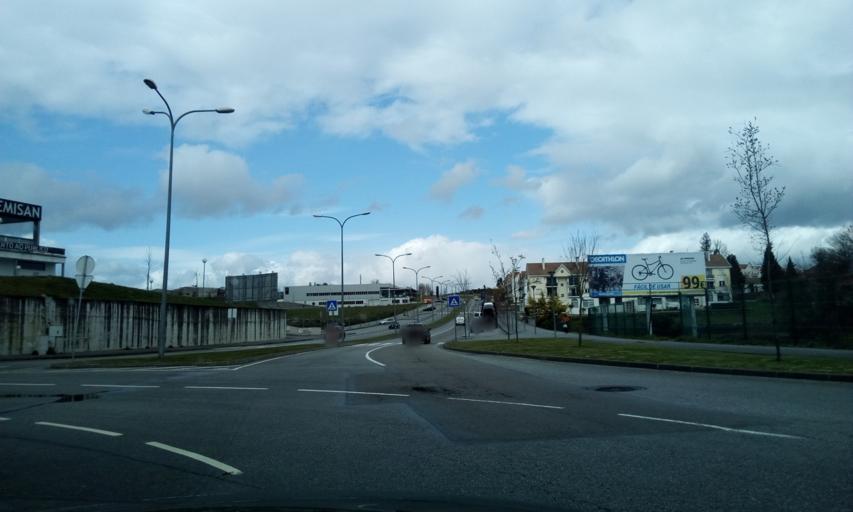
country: PT
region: Viseu
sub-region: Viseu
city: Viseu
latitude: 40.6303
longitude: -7.9107
